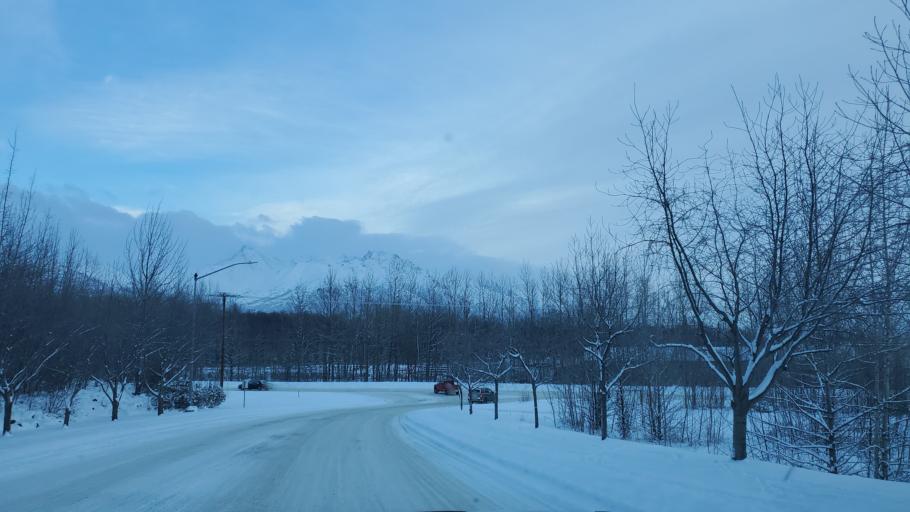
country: US
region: Alaska
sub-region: Matanuska-Susitna Borough
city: Palmer
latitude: 61.5942
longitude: -149.1199
